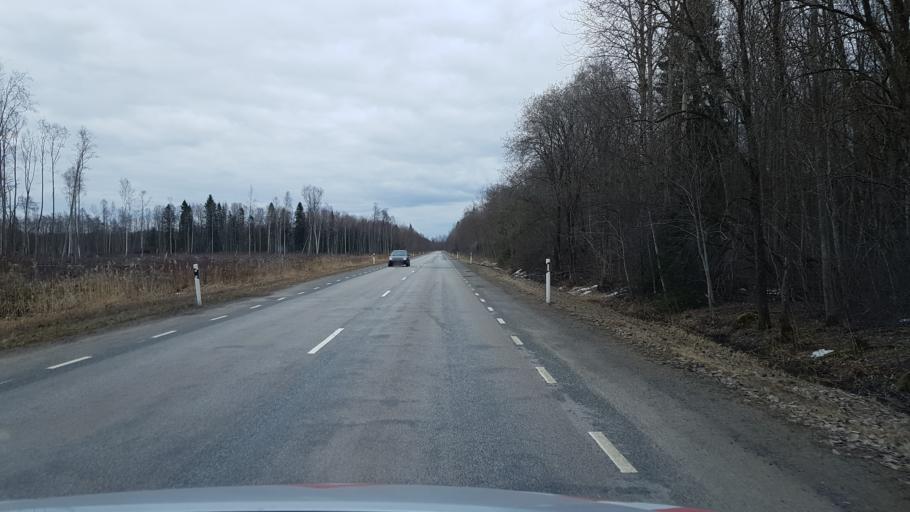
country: EE
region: Ida-Virumaa
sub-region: Narva-Joesuu linn
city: Narva-Joesuu
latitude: 59.3526
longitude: 28.0765
